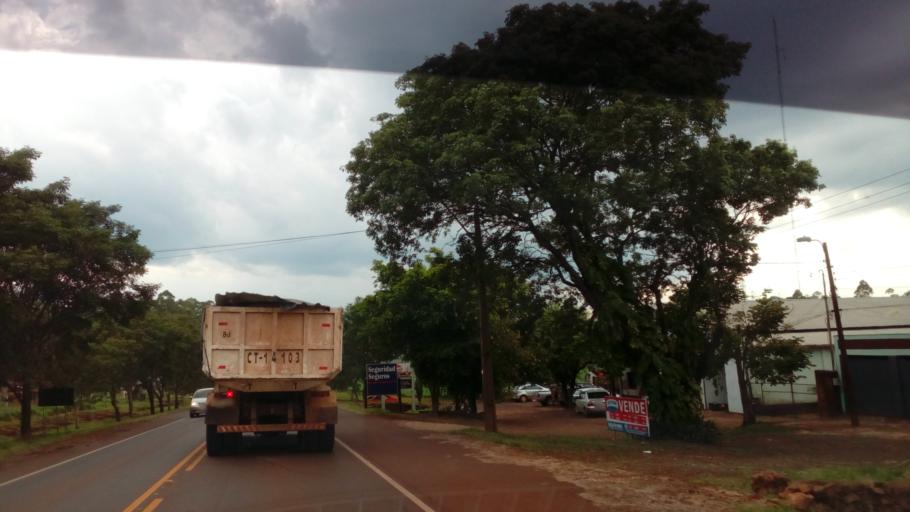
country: PY
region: Itapua
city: Obligado
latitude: -27.0712
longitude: -55.6141
